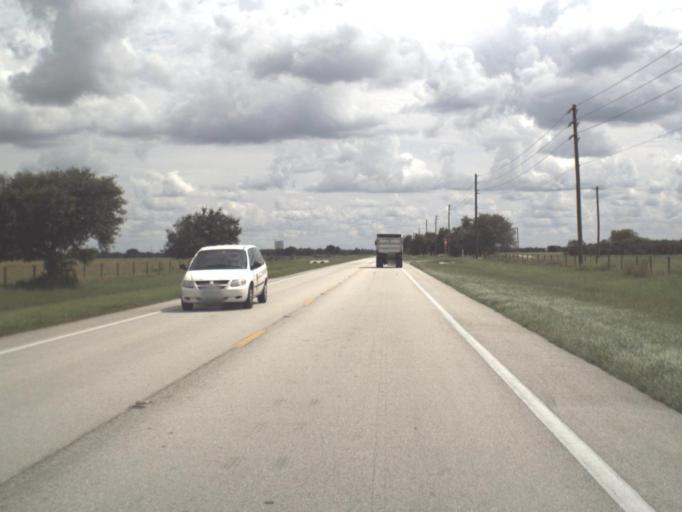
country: US
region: Florida
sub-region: DeSoto County
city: Nocatee
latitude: 27.0425
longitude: -81.7779
